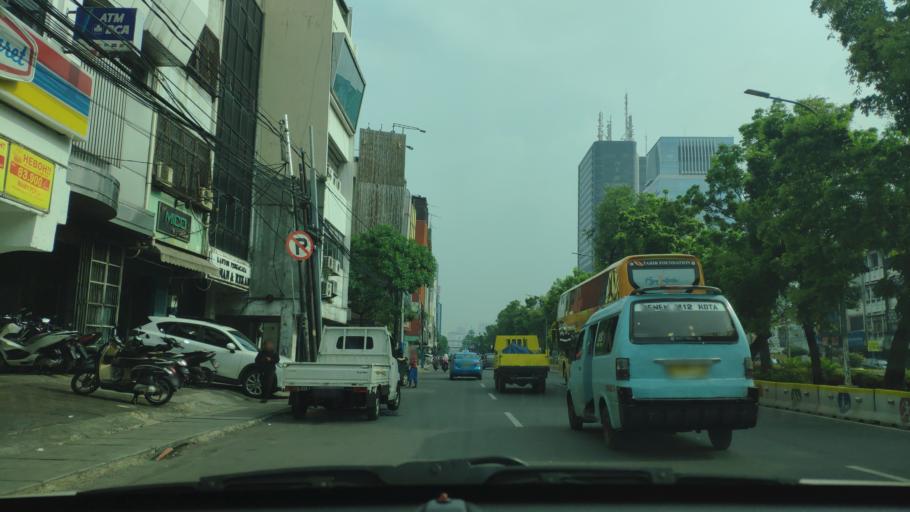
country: ID
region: Jakarta Raya
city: Jakarta
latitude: -6.1572
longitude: 106.8187
